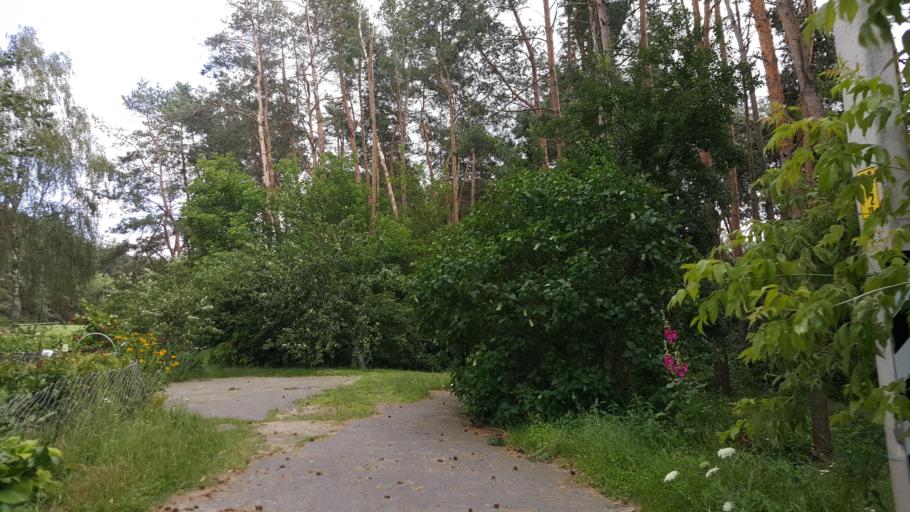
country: BY
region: Brest
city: Kamyanyets
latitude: 52.3921
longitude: 23.8355
